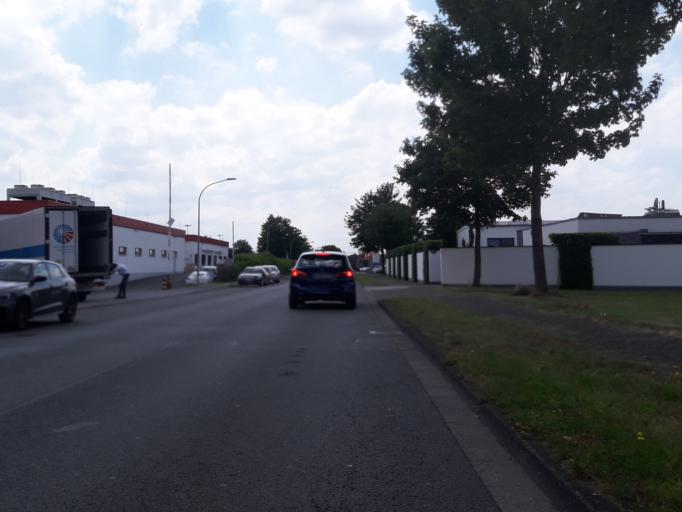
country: DE
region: North Rhine-Westphalia
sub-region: Regierungsbezirk Detmold
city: Paderborn
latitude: 51.7359
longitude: 8.7830
